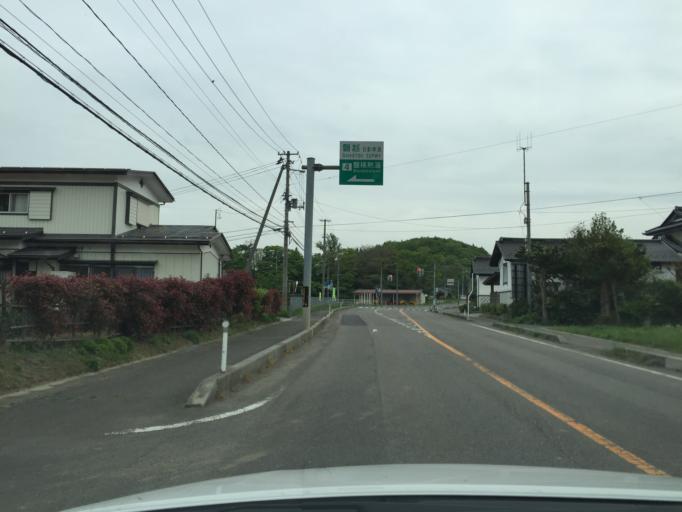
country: JP
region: Fukushima
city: Motomiya
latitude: 37.4972
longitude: 140.2803
